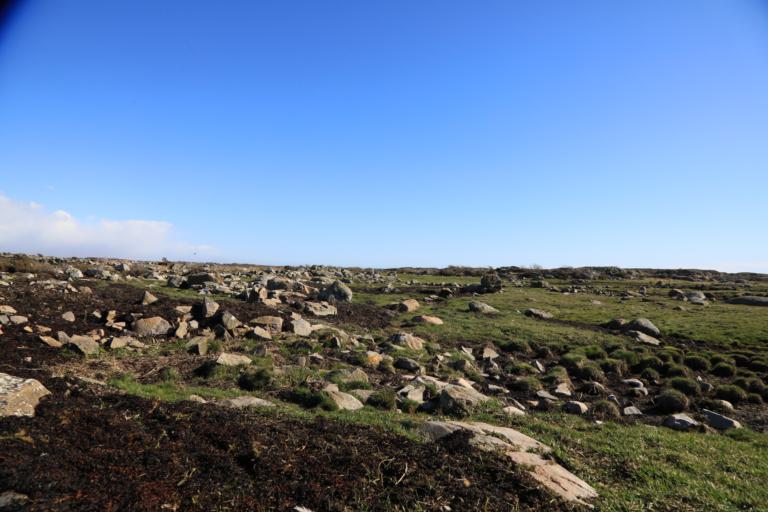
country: SE
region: Halland
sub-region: Varbergs Kommun
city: Traslovslage
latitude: 57.0653
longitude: 12.2518
